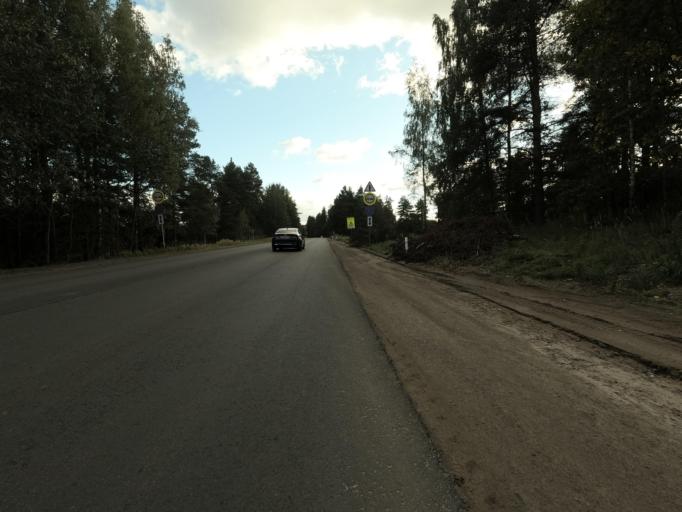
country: RU
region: Leningrad
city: Koltushi
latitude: 59.9631
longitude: 30.6584
